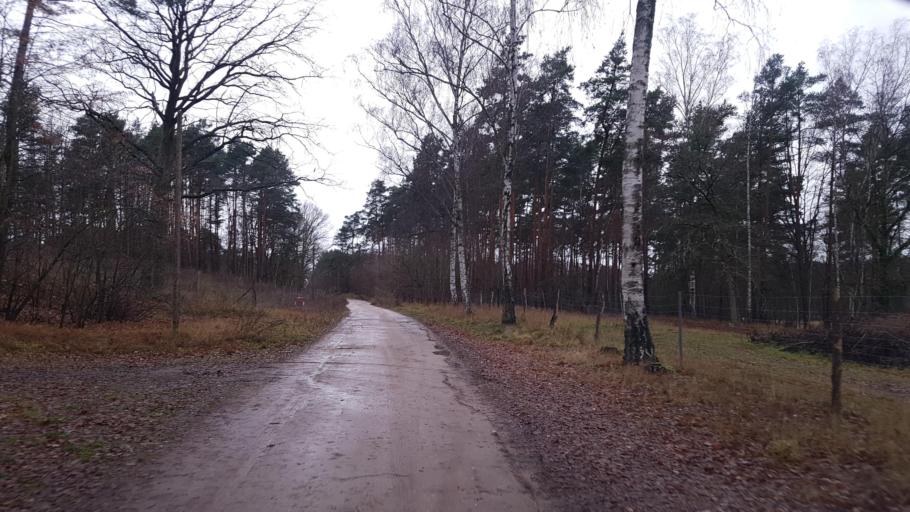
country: DE
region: Brandenburg
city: Luebben
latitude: 51.9333
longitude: 13.8524
